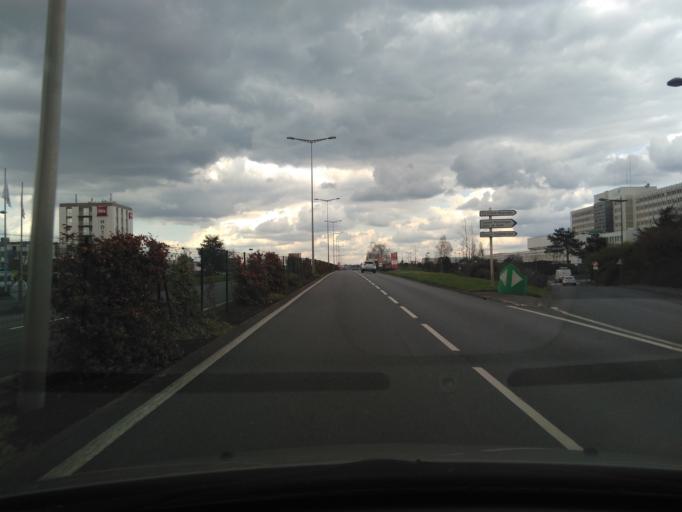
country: FR
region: Pays de la Loire
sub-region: Departement de Maine-et-Loire
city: Cholet
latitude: 47.0415
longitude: -0.9000
